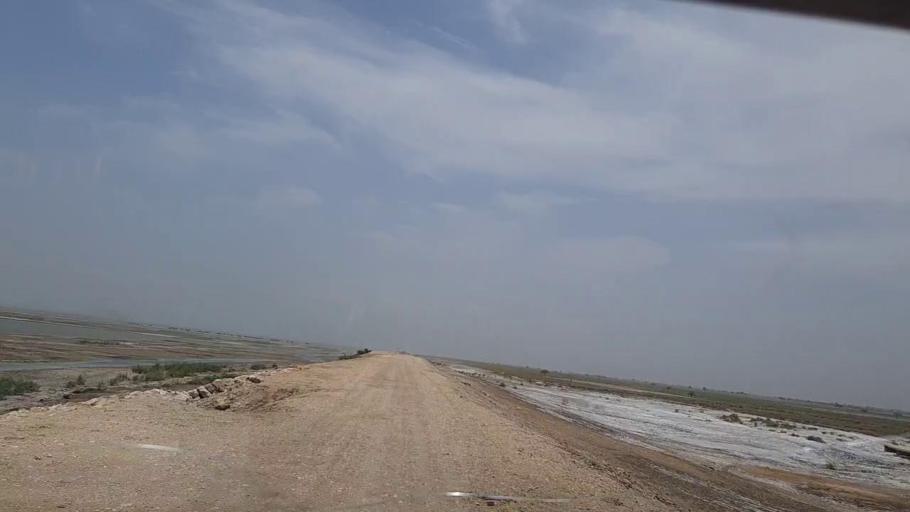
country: PK
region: Sindh
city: Sehwan
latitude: 26.4160
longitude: 67.7548
